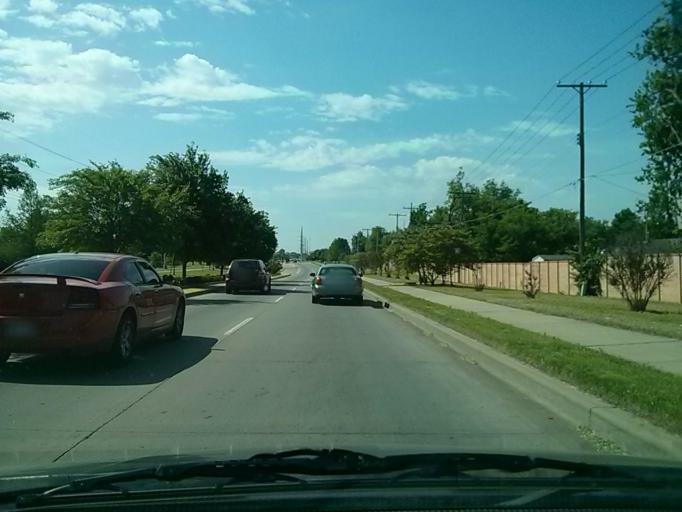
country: US
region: Oklahoma
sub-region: Tulsa County
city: Tulsa
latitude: 36.1831
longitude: -95.9760
